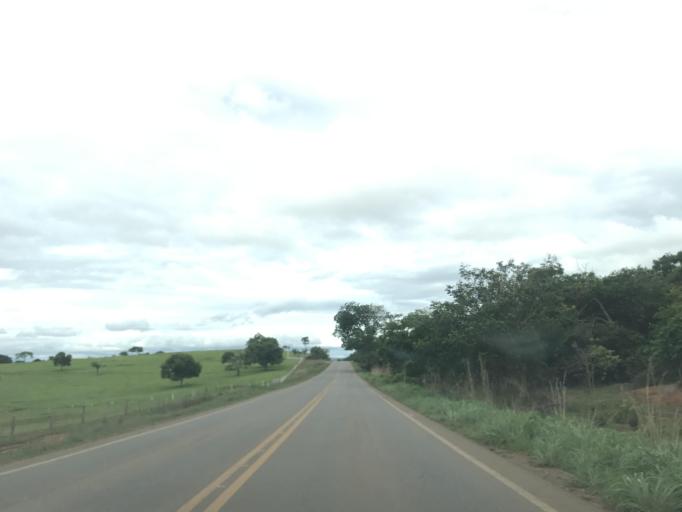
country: BR
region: Goias
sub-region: Vianopolis
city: Vianopolis
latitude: -16.7060
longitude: -48.3937
